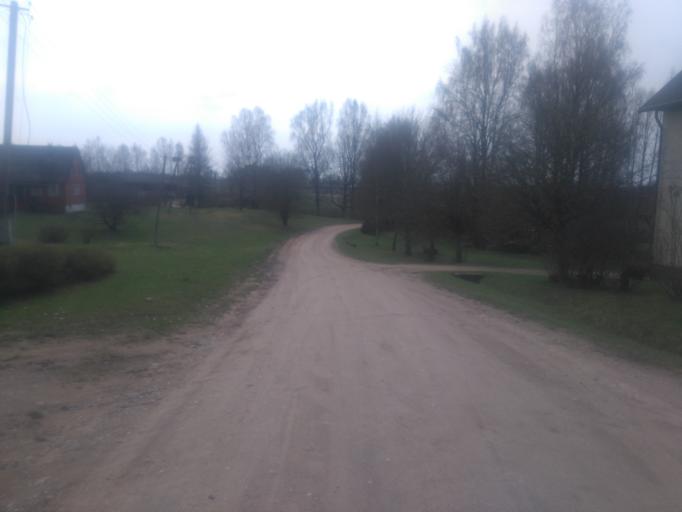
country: LV
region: Vecpiebalga
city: Vecpiebalga
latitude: 57.0249
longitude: 25.8470
